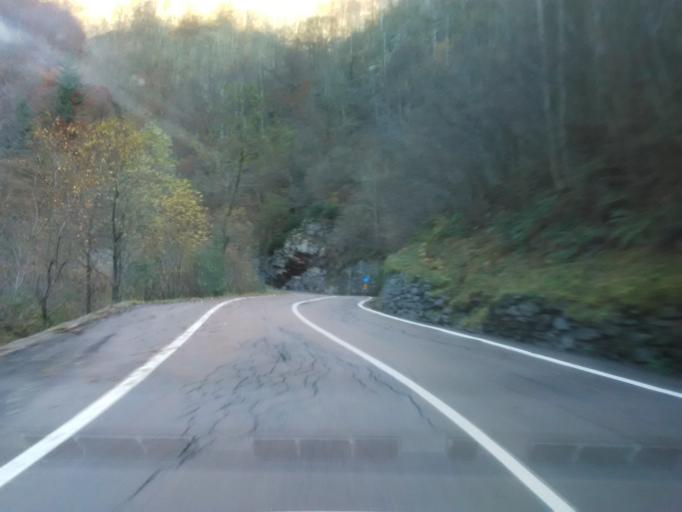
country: IT
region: Piedmont
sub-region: Provincia di Vercelli
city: Cervatto
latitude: 45.8804
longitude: 8.1792
